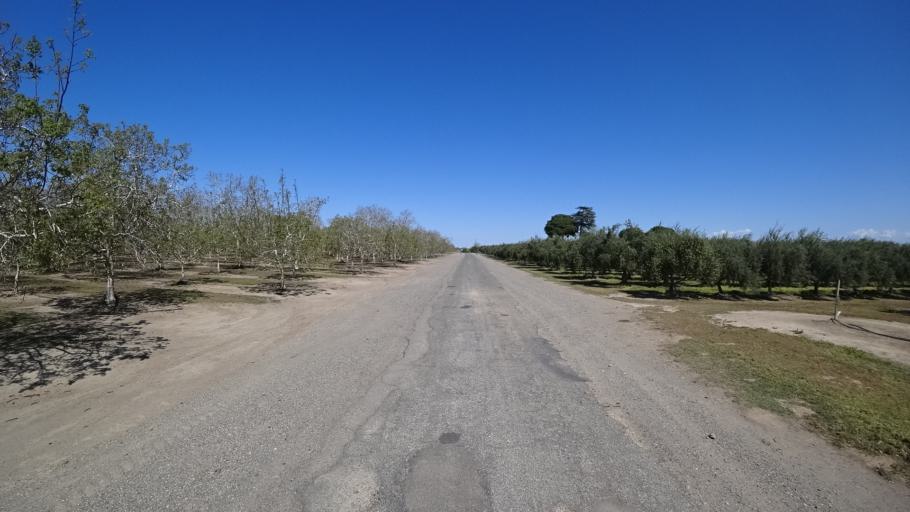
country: US
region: California
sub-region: Glenn County
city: Orland
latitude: 39.7083
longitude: -122.1456
